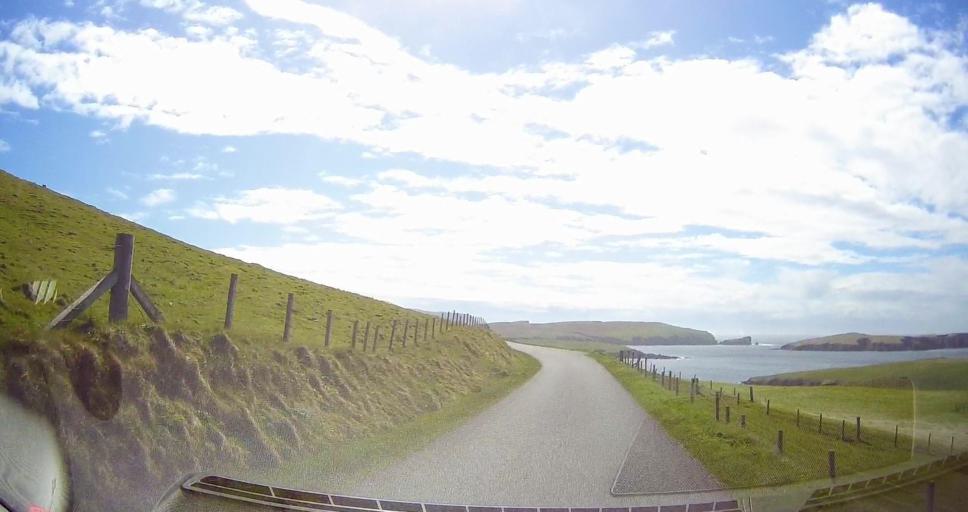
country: GB
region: Scotland
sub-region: Shetland Islands
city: Sandwick
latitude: 59.9548
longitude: -1.3266
